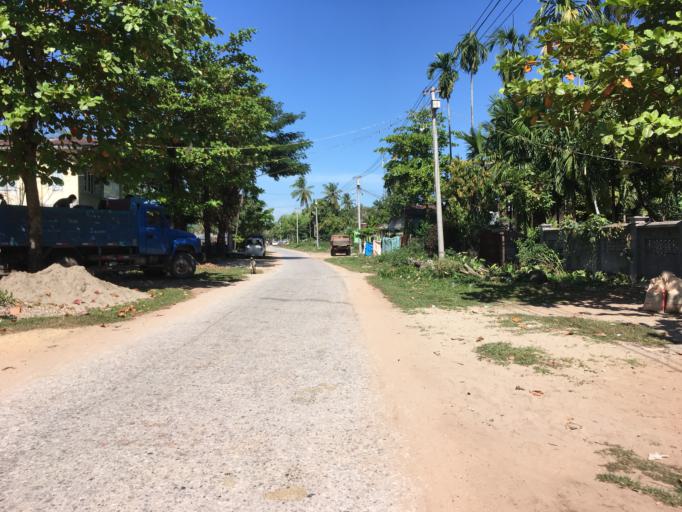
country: MM
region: Mon
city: Mawlamyine
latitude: 16.4524
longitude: 97.6299
